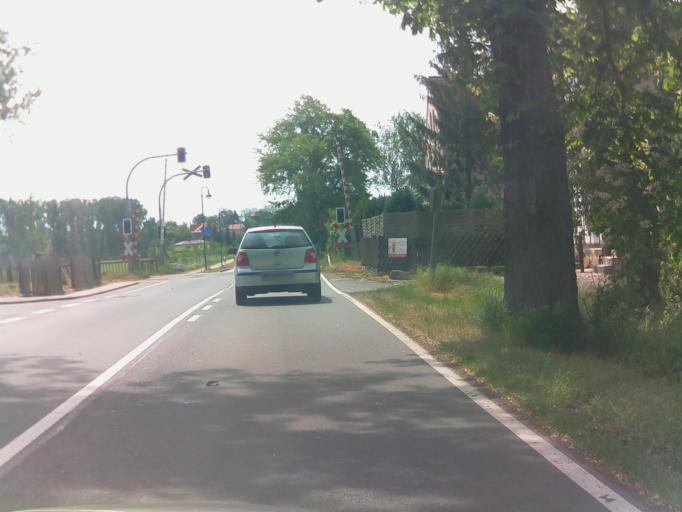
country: DE
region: Saxony-Anhalt
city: Hedersleben
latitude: 51.8459
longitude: 11.2501
